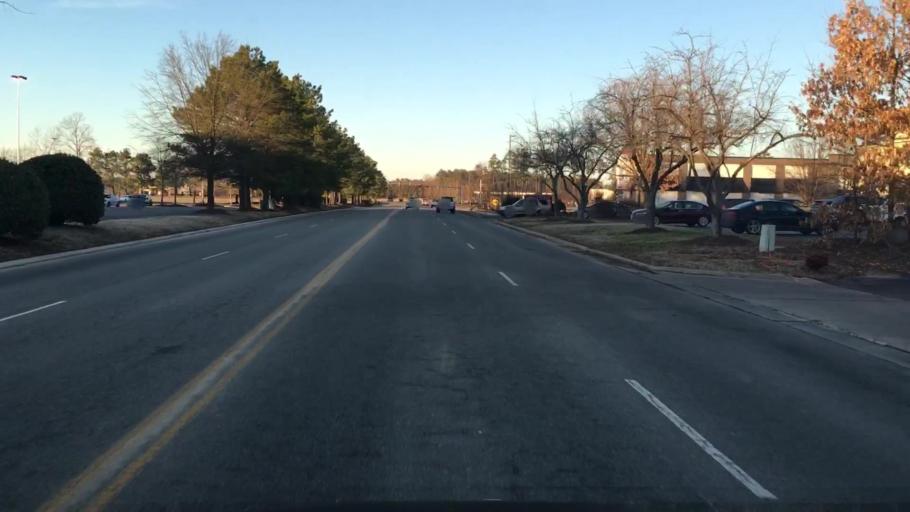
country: US
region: Virginia
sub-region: Chesterfield County
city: Bon Air
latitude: 37.5090
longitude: -77.6065
